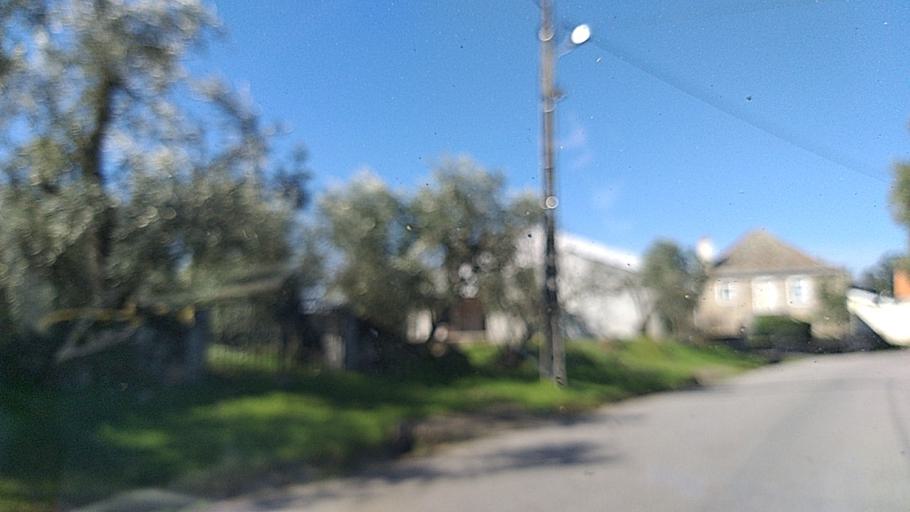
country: PT
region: Guarda
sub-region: Fornos de Algodres
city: Fornos de Algodres
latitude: 40.5932
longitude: -7.4673
